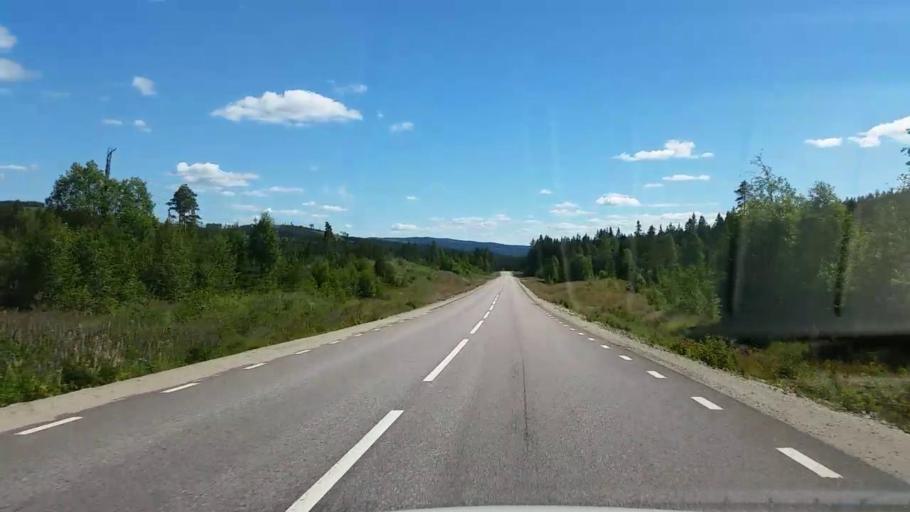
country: SE
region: Gaevleborg
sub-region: Bollnas Kommun
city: Vittsjo
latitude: 61.0679
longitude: 15.7962
